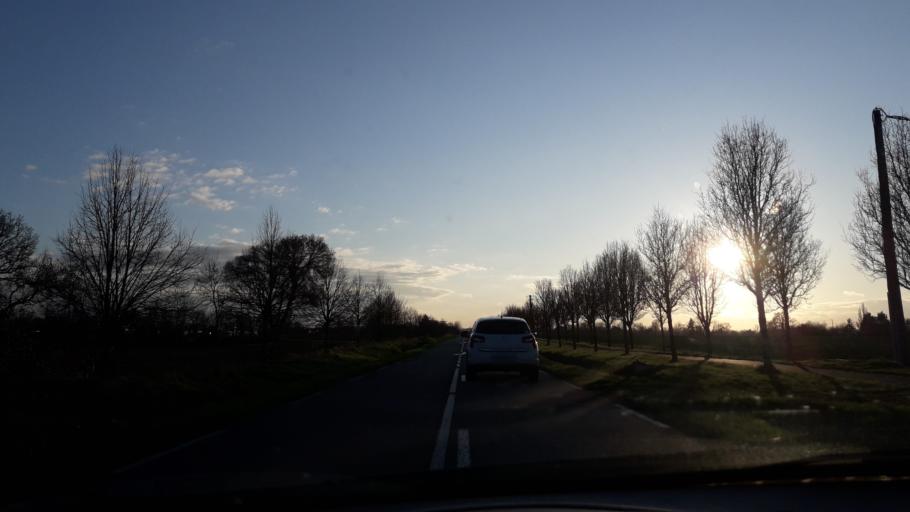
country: FR
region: Midi-Pyrenees
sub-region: Departement de la Haute-Garonne
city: Levignac
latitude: 43.6492
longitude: 1.1695
